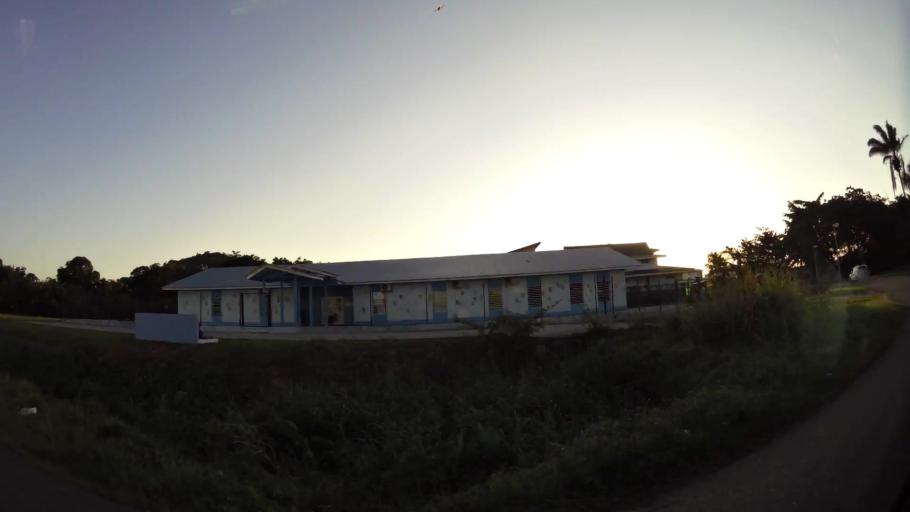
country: GF
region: Guyane
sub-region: Guyane
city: Cayenne
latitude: 4.9267
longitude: -52.3021
